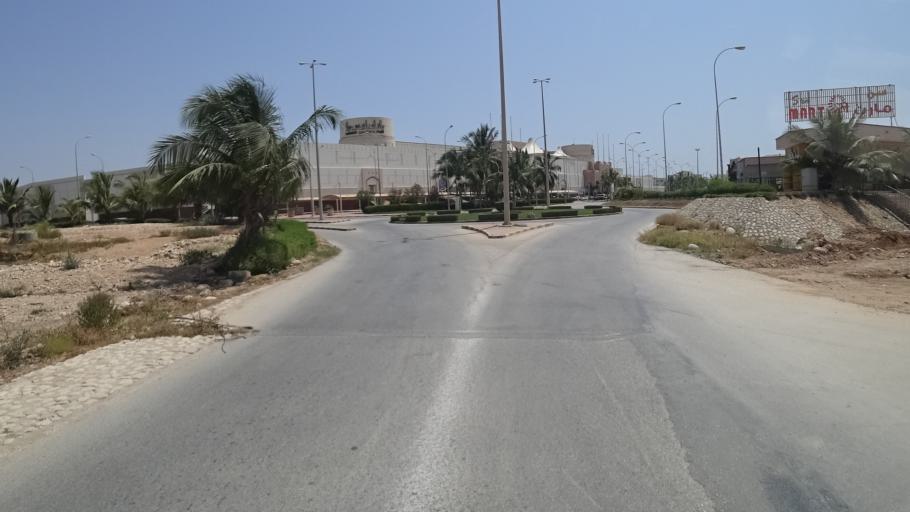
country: OM
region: Zufar
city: Salalah
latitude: 17.0235
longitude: 54.0635
